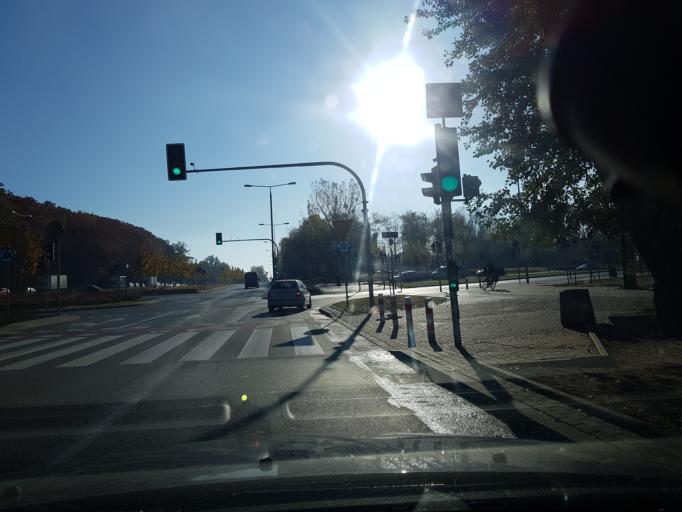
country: PL
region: Masovian Voivodeship
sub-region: Warszawa
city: Bielany
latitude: 52.2858
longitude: 20.9402
